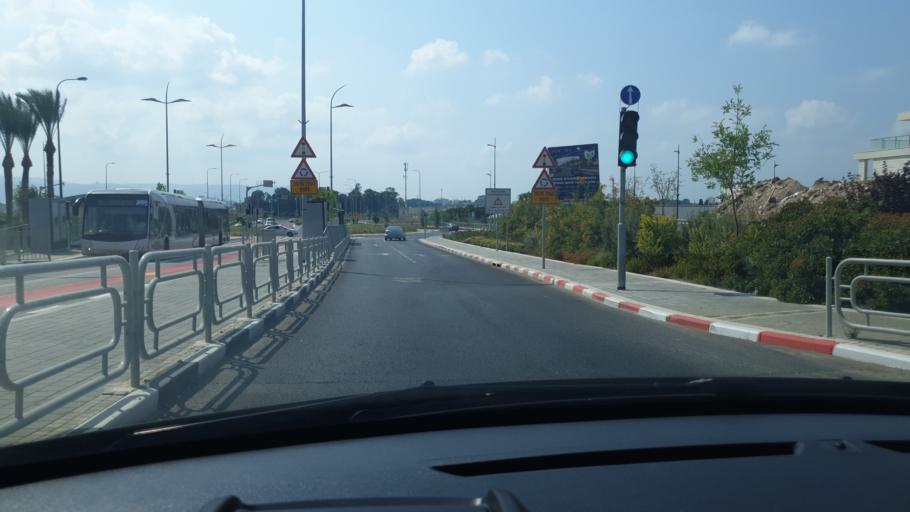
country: IL
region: Haifa
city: Qiryat Ata
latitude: 32.8128
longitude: 35.1013
